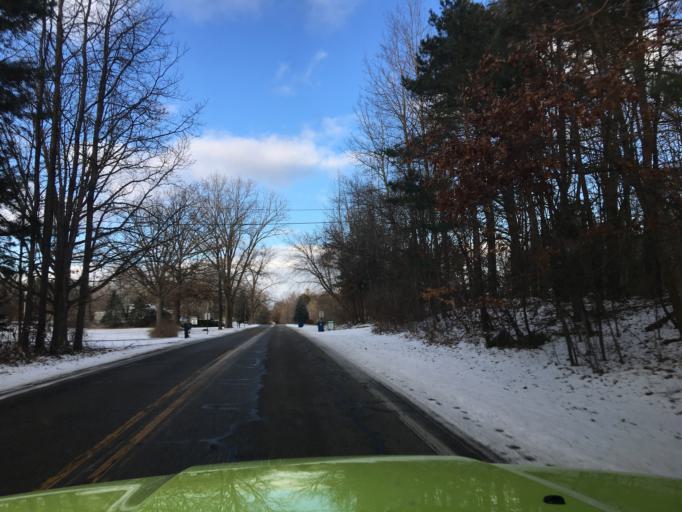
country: US
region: Michigan
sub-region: Montcalm County
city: Greenville
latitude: 43.1849
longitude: -85.2830
